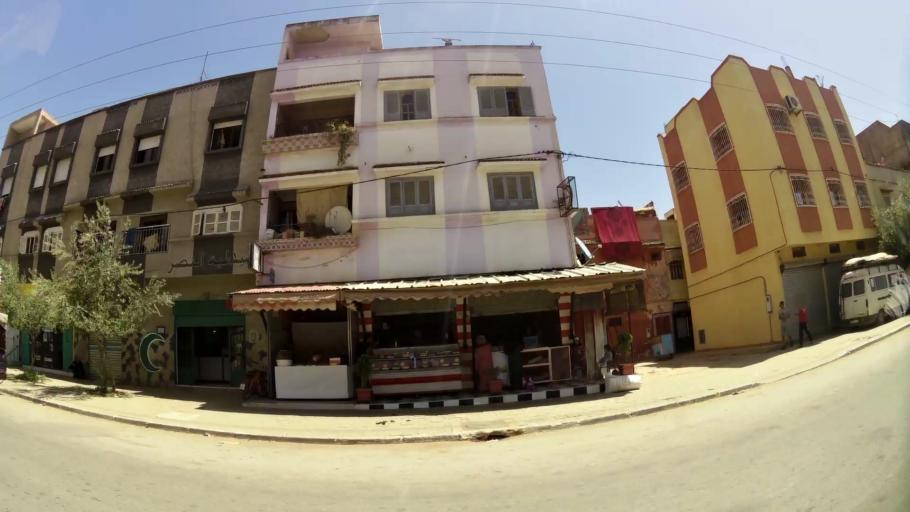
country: MA
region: Rabat-Sale-Zemmour-Zaer
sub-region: Khemisset
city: Khemisset
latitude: 33.8345
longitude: -6.0661
